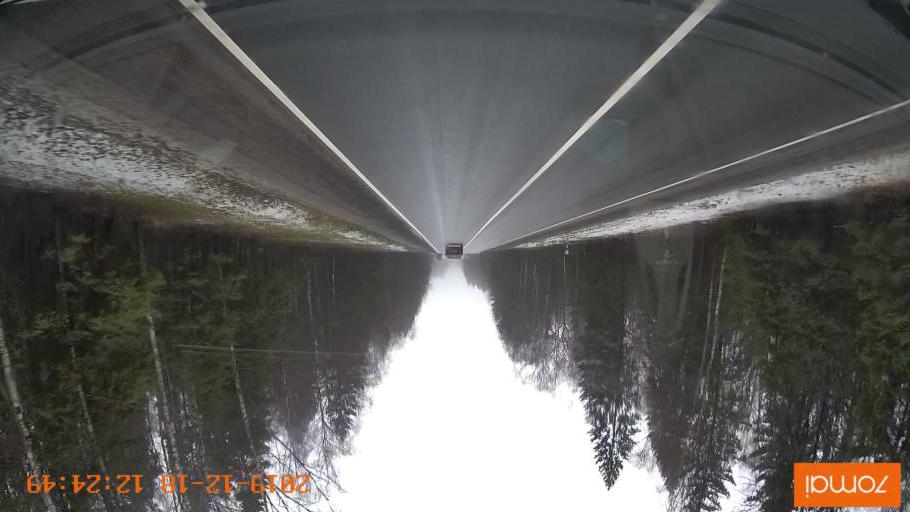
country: RU
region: Moskovskaya
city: Novopetrovskoye
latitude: 56.0297
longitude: 36.5006
